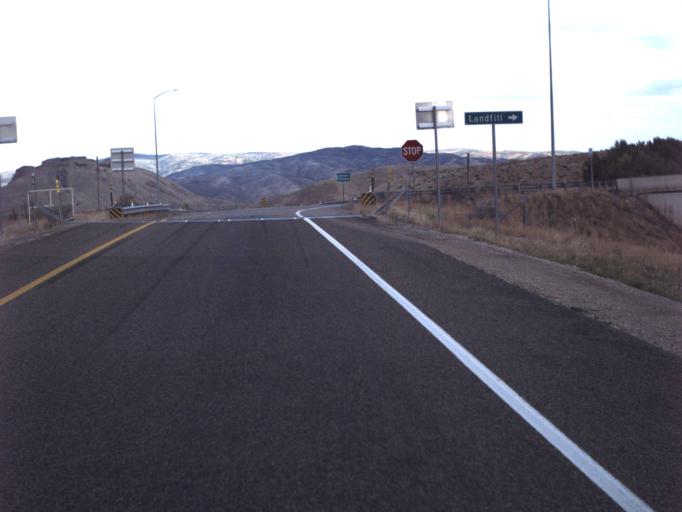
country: US
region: Utah
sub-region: Summit County
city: Coalville
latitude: 41.0154
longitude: -111.4889
